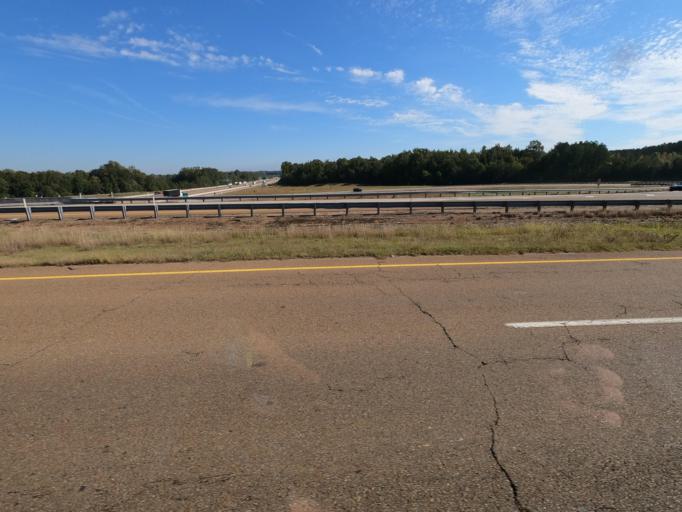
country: US
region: Tennessee
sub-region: Shelby County
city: Arlington
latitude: 35.2552
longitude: -89.6767
